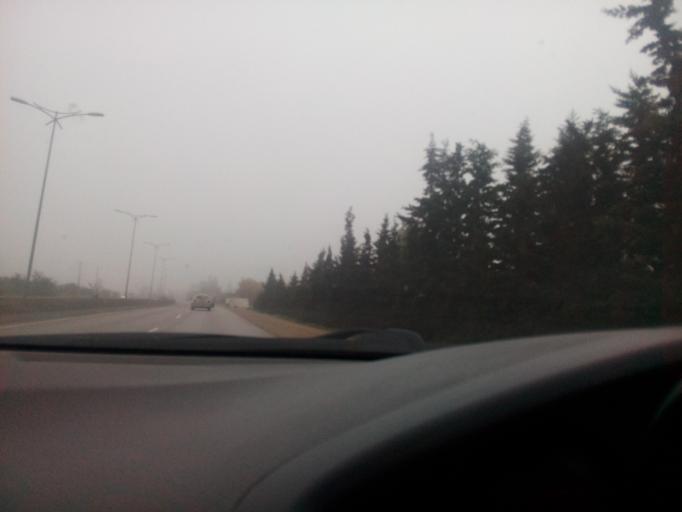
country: DZ
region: Oran
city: Bou Tlelis
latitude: 35.5727
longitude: -0.8615
